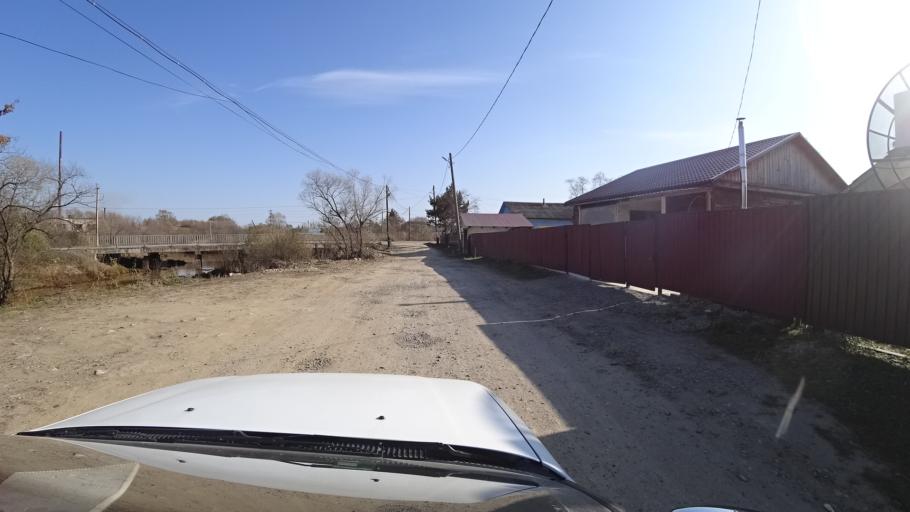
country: RU
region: Primorskiy
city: Dal'nerechensk
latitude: 45.9252
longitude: 133.7258
